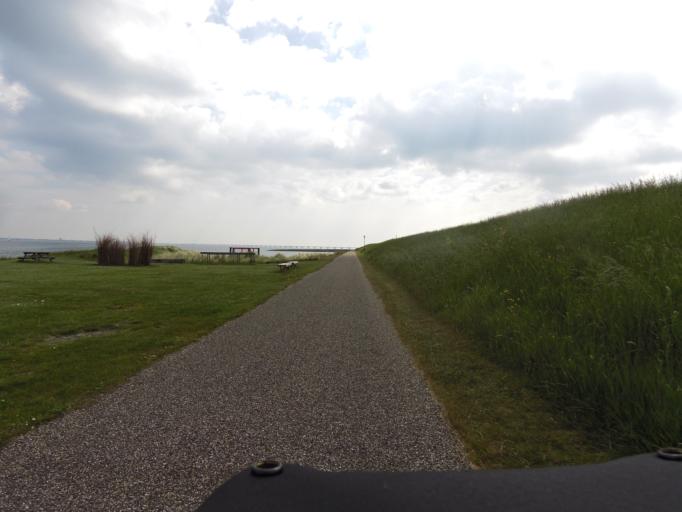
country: NL
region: Zeeland
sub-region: Gemeente Goes
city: Goes
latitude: 51.6049
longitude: 3.8329
